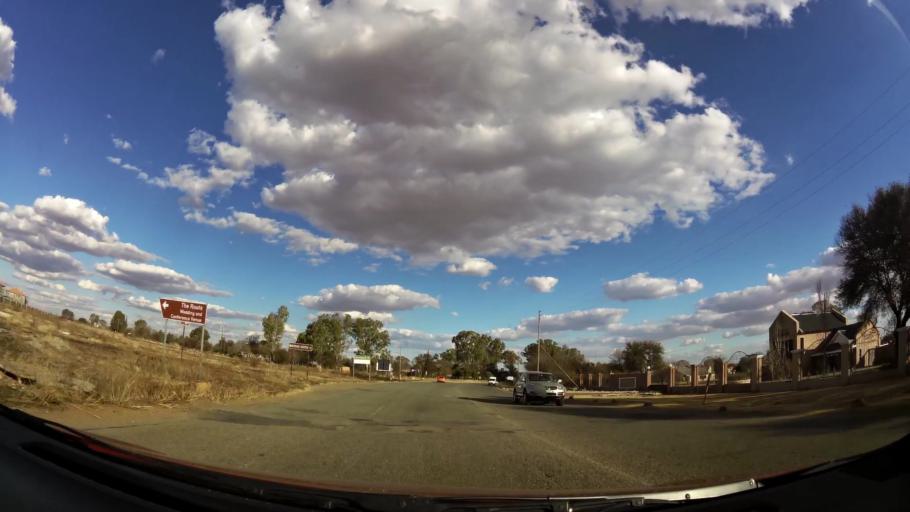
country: ZA
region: North-West
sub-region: Dr Kenneth Kaunda District Municipality
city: Potchefstroom
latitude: -26.6715
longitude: 27.1061
